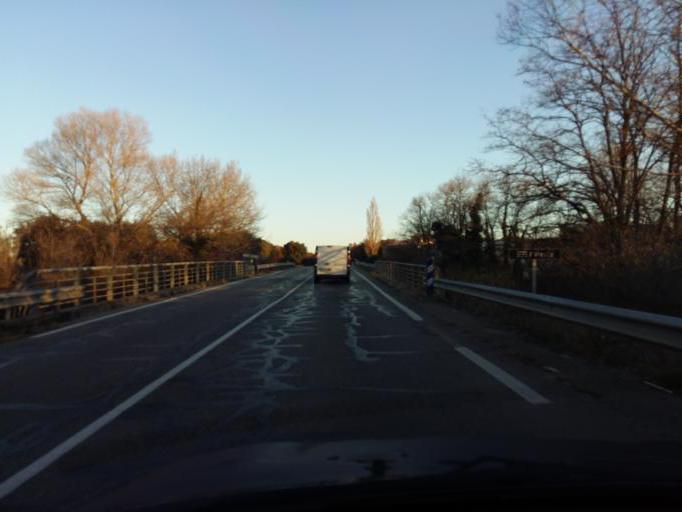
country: FR
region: Provence-Alpes-Cote d'Azur
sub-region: Departement du Vaucluse
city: Visan
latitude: 44.3380
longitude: 4.9479
